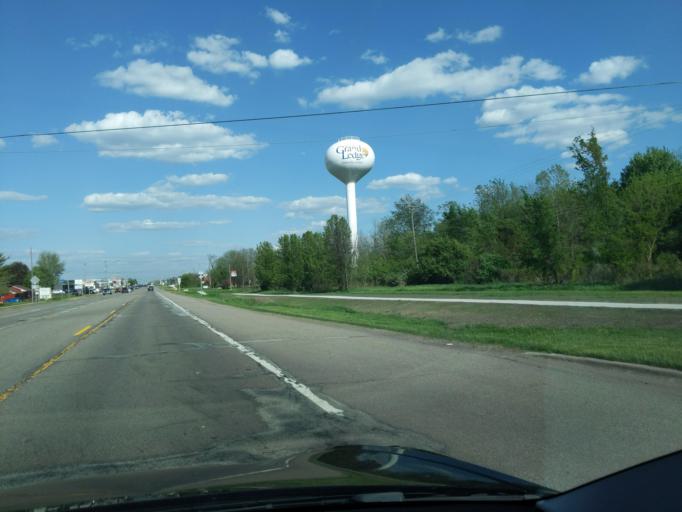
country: US
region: Michigan
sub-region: Eaton County
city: Grand Ledge
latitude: 42.7408
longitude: -84.7487
